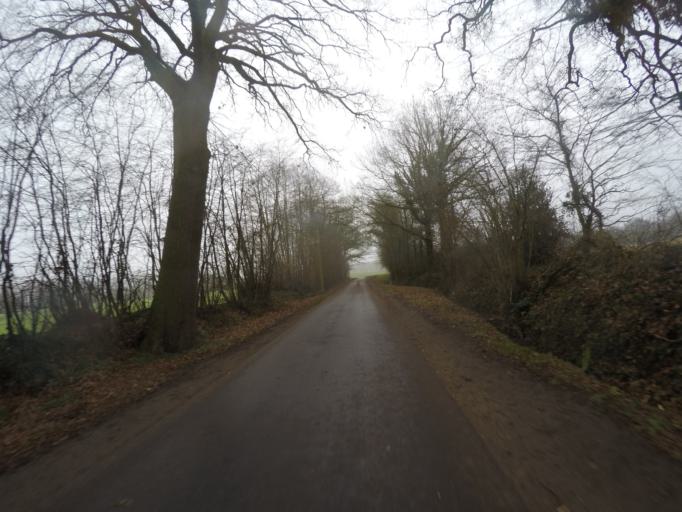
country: DE
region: Schleswig-Holstein
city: Bilsen
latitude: 53.7544
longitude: 9.8912
